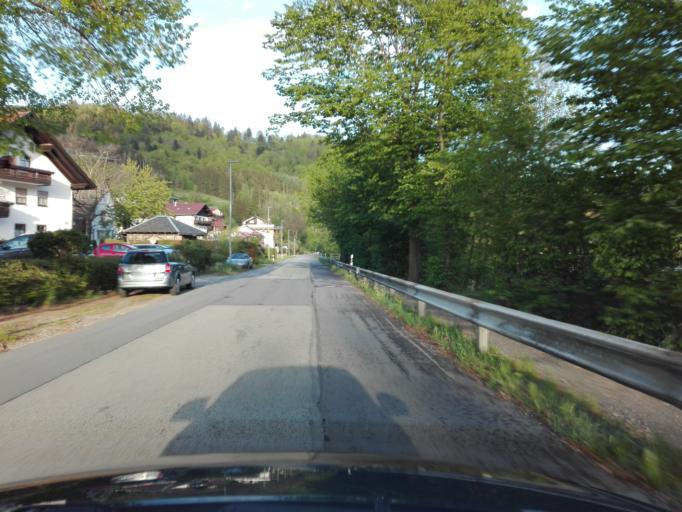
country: DE
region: Bavaria
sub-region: Lower Bavaria
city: Obernzell
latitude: 48.5527
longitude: 13.6465
